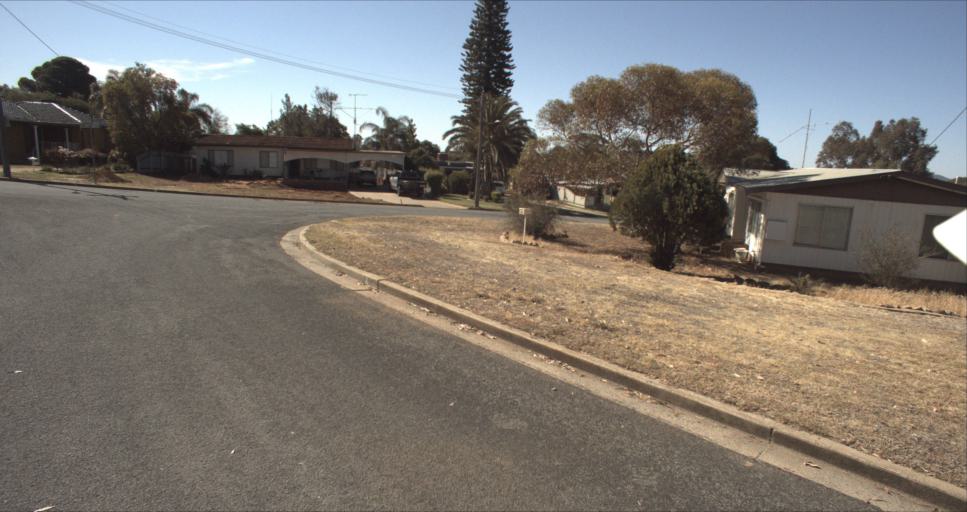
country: AU
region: New South Wales
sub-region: Leeton
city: Leeton
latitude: -34.5501
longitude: 146.3772
